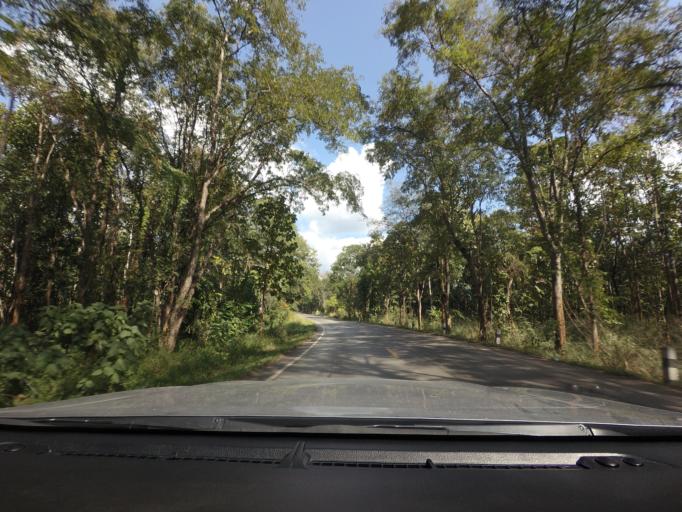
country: TH
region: Chiang Mai
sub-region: Amphoe Chiang Dao
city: Chiang Dao
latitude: 19.4923
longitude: 99.0326
